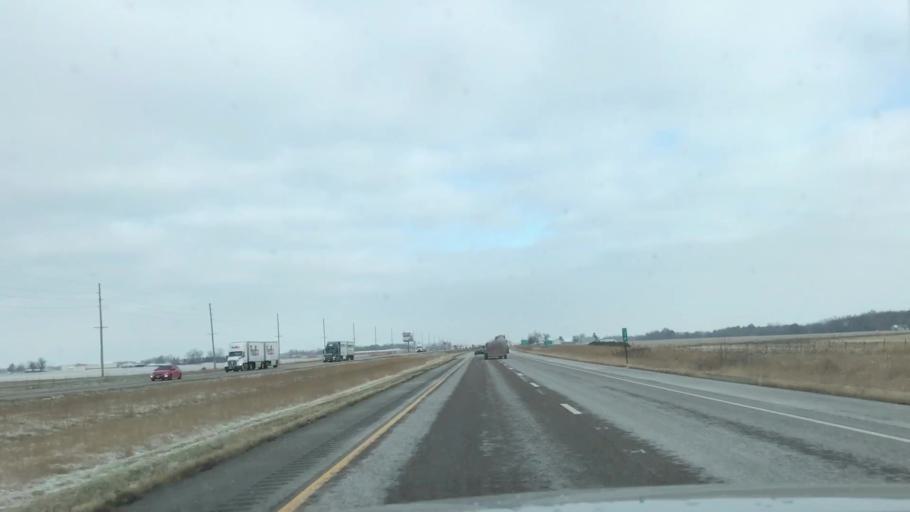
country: US
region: Illinois
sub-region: Macoupin County
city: Staunton
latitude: 38.9967
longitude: -89.7497
